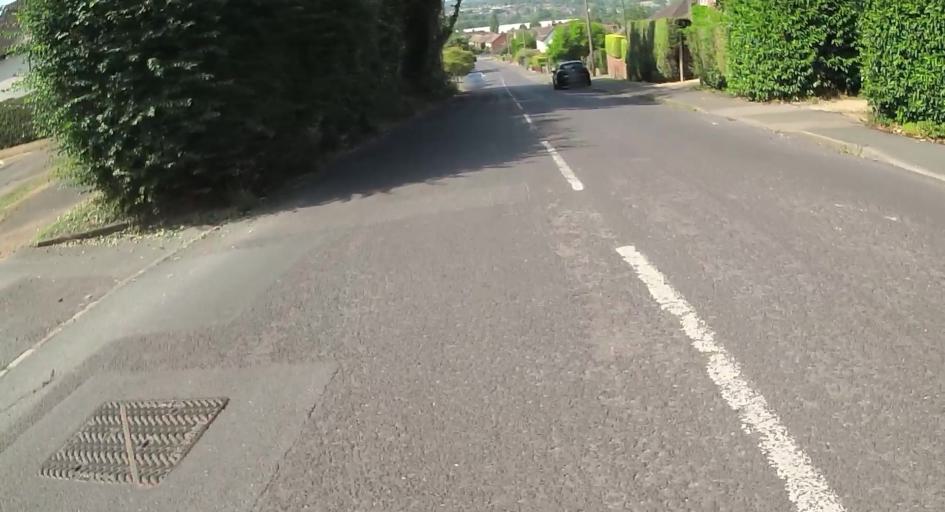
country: GB
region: England
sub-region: Surrey
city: Farnham
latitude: 51.2006
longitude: -0.8068
